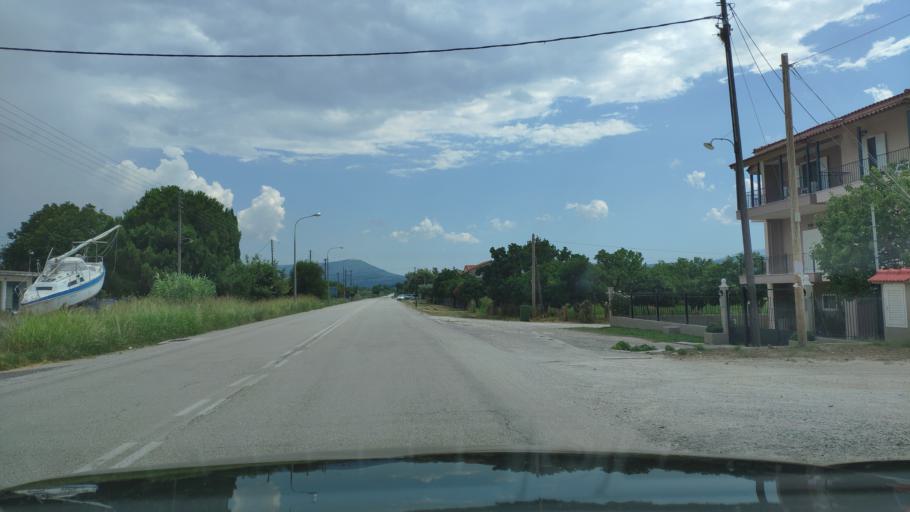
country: GR
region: West Greece
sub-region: Nomos Aitolias kai Akarnanias
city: Krikellos
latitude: 38.9455
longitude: 21.1764
